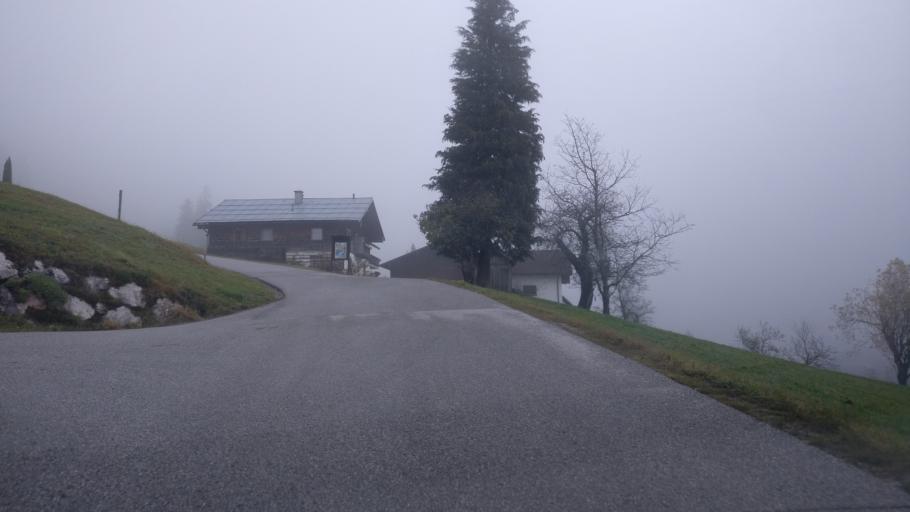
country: AT
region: Salzburg
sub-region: Politischer Bezirk Sankt Johann im Pongau
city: Filzmoos
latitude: 47.4023
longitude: 13.5291
